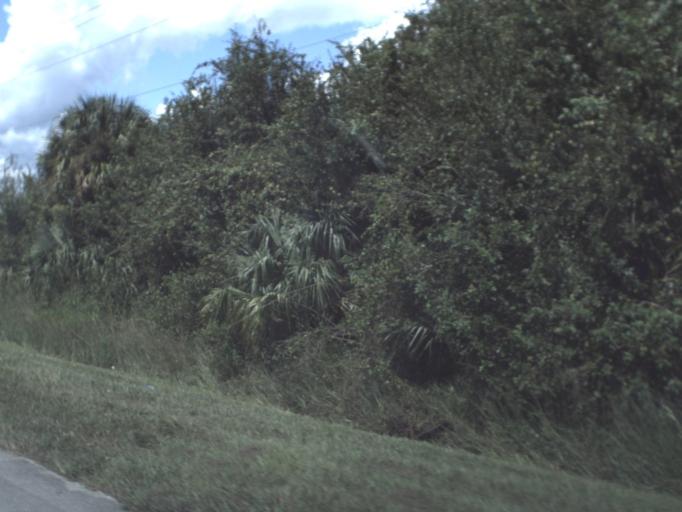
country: US
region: Florida
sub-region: Okeechobee County
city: Taylor Creek
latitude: 27.2196
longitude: -80.7637
